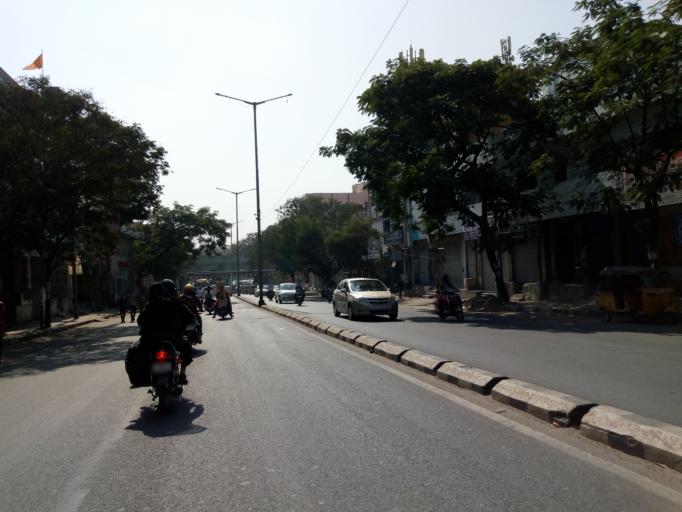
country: IN
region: Telangana
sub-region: Hyderabad
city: Malkajgiri
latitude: 17.4327
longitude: 78.4931
